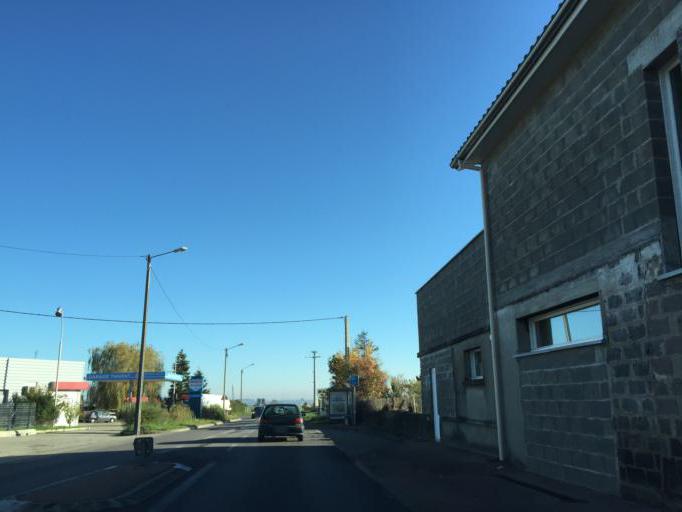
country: FR
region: Rhone-Alpes
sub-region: Departement du Rhone
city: Saint-Andeol-le-Chateau
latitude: 45.5891
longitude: 4.6664
